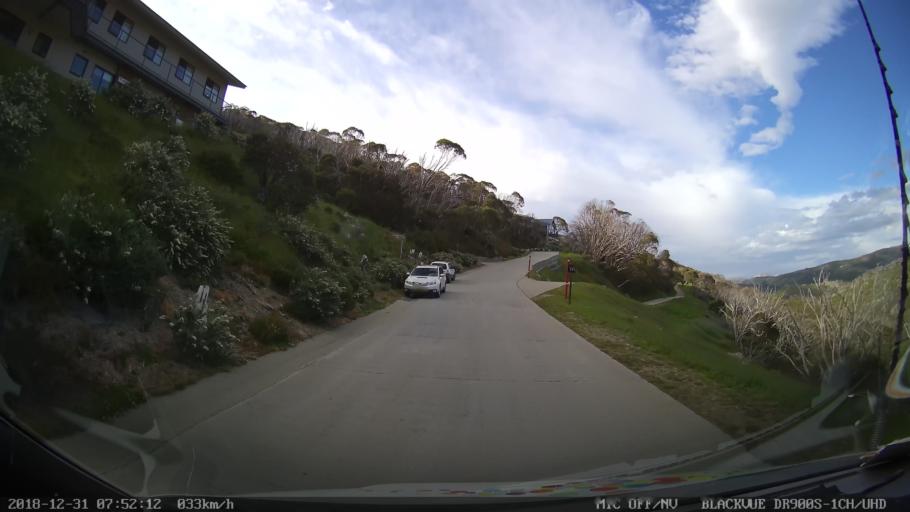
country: AU
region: New South Wales
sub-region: Snowy River
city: Jindabyne
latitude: -36.3798
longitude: 148.3737
